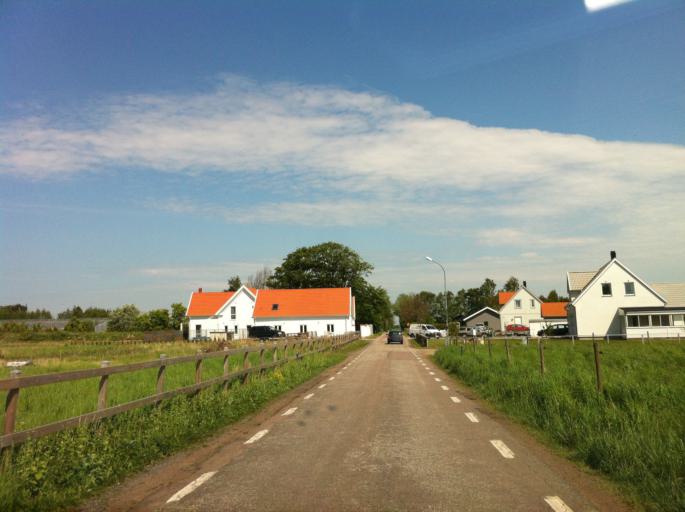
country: SE
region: Skane
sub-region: Landskrona
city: Landskrona
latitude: 55.9179
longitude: 12.8698
